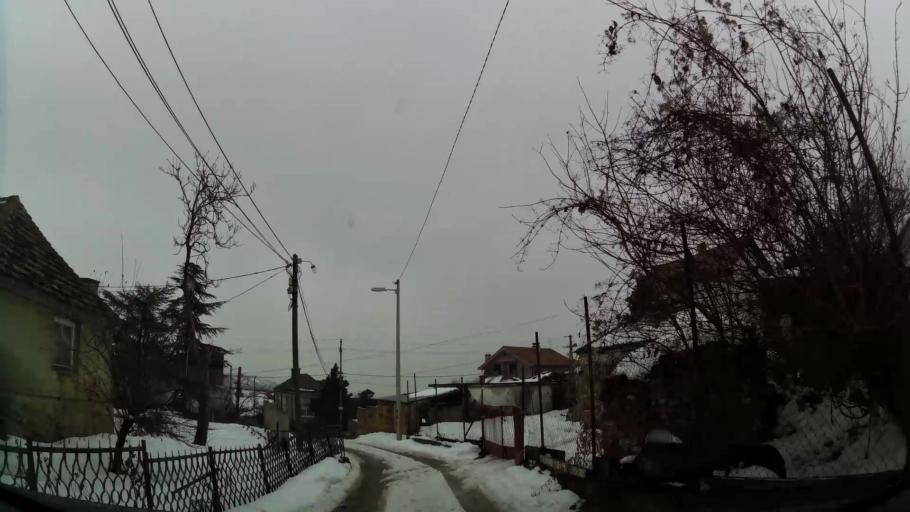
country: RS
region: Central Serbia
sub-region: Belgrade
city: Zvezdara
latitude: 44.7426
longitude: 20.5154
